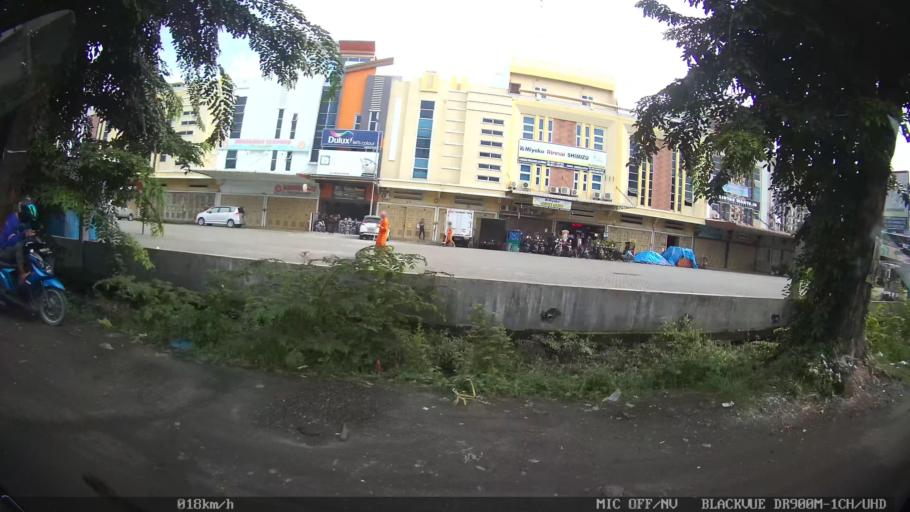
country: ID
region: North Sumatra
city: Medan
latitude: 3.6287
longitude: 98.7029
